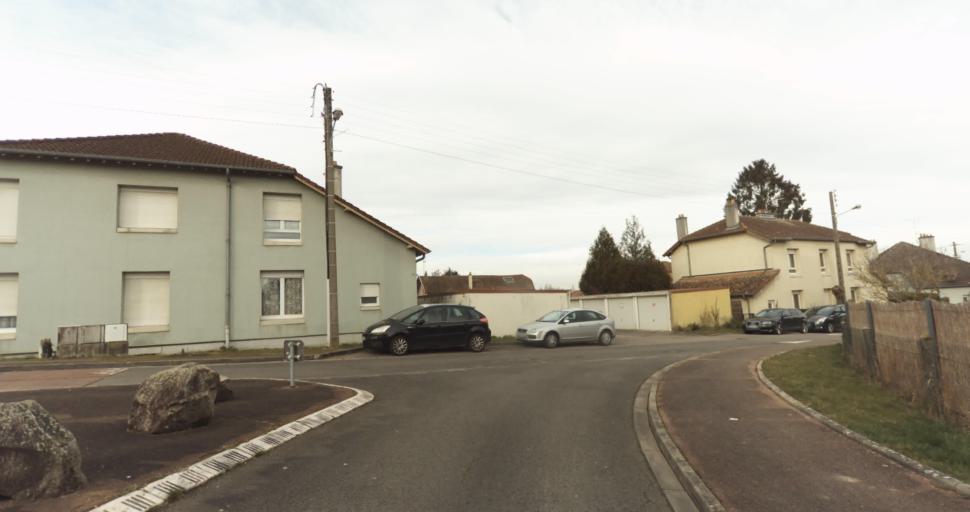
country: FR
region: Lorraine
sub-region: Departement de Meurthe-et-Moselle
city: Jarny
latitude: 49.1641
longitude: 5.8778
